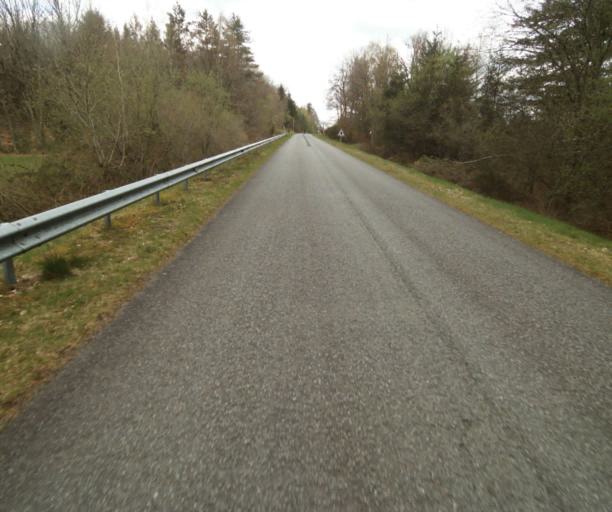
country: FR
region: Limousin
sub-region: Departement de la Correze
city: Correze
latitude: 45.3586
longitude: 1.9267
